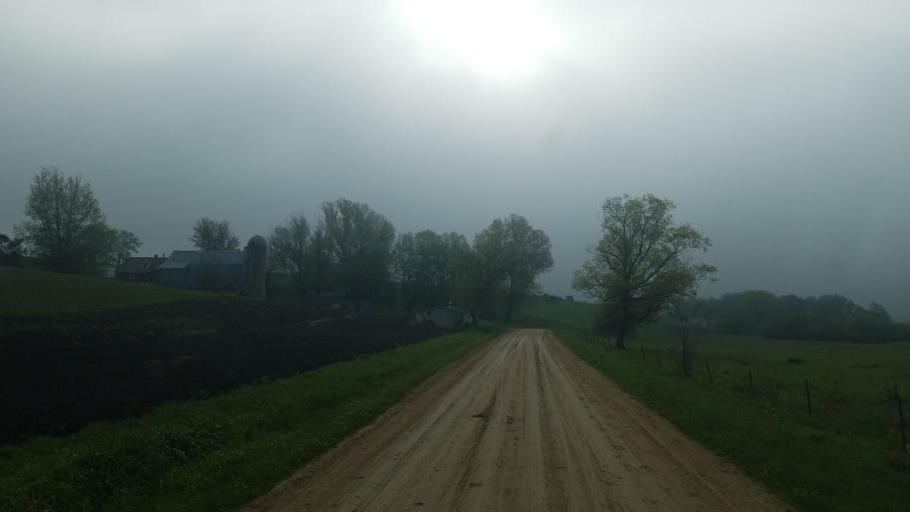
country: US
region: Wisconsin
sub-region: Vernon County
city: Hillsboro
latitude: 43.6239
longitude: -90.3903
